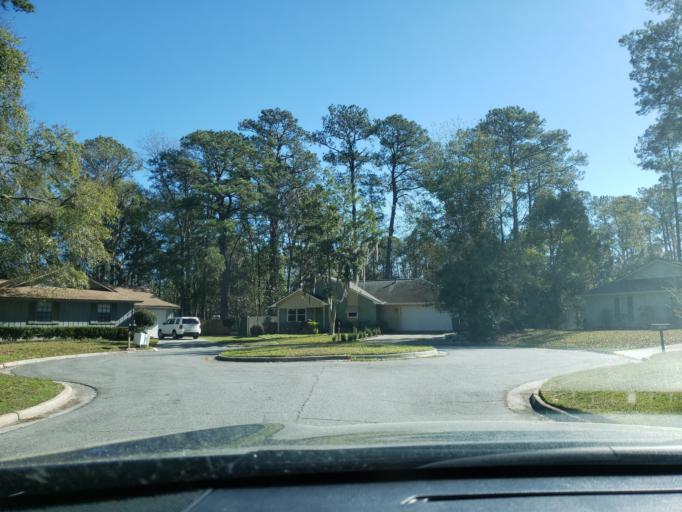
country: US
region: Georgia
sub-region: Chatham County
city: Isle of Hope
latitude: 31.9843
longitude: -81.0618
